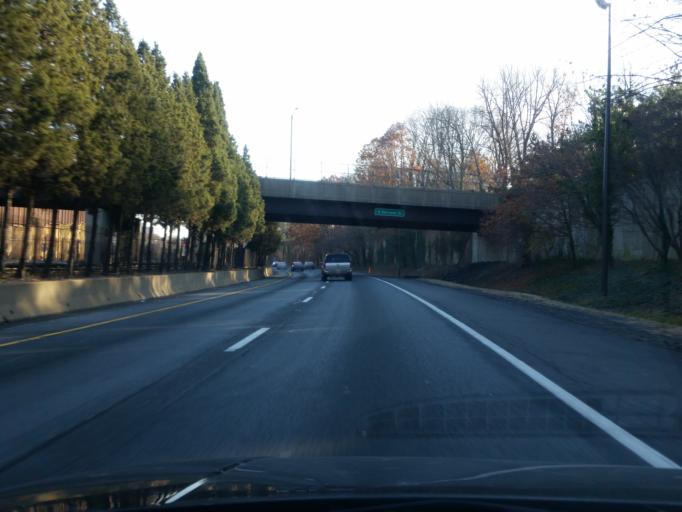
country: US
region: Virginia
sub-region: Arlington County
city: Arlington
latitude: 38.8794
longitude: -77.1288
